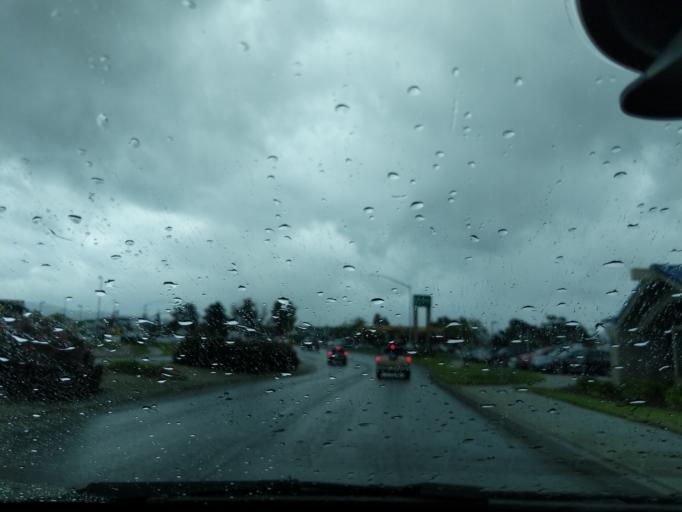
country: US
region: California
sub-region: Monterey County
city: Boronda
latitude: 36.6977
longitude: -121.6684
